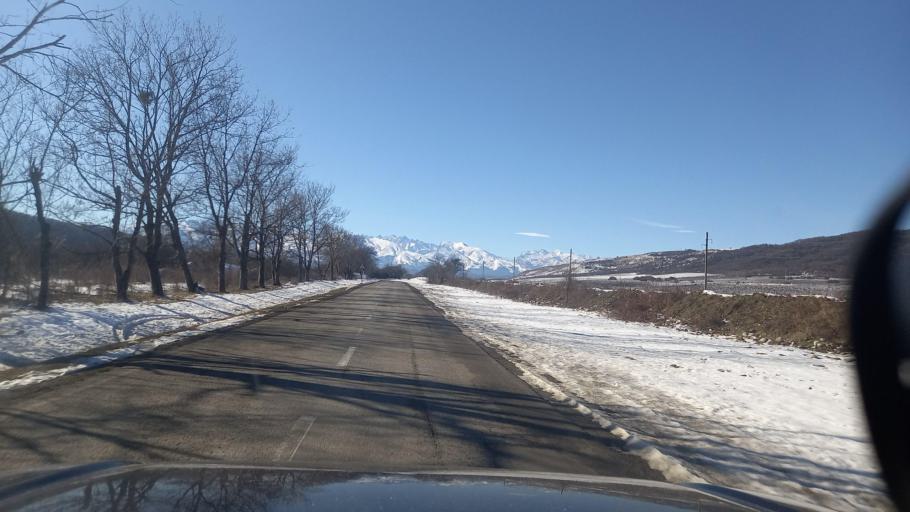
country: RU
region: North Ossetia
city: Chikola
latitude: 43.2462
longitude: 43.9623
